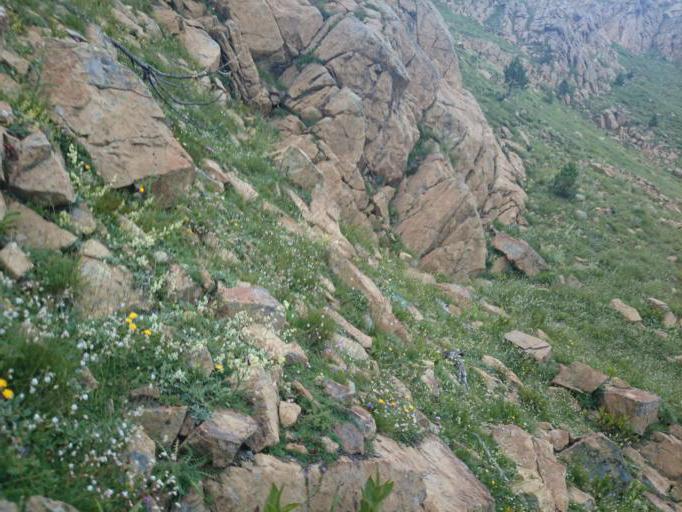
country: AL
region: Diber
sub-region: Rrethi i Dibres
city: Fushe-Lure
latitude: 41.7828
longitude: 20.1830
